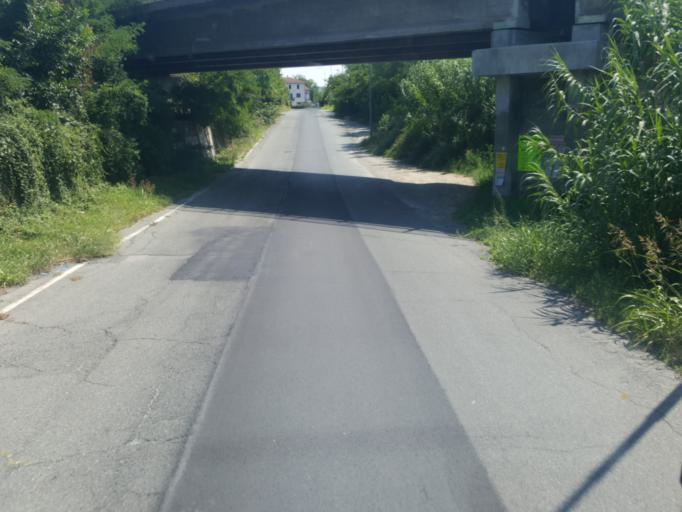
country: IT
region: Piedmont
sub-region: Provincia di Alessandria
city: Visone
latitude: 44.6804
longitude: 8.4909
